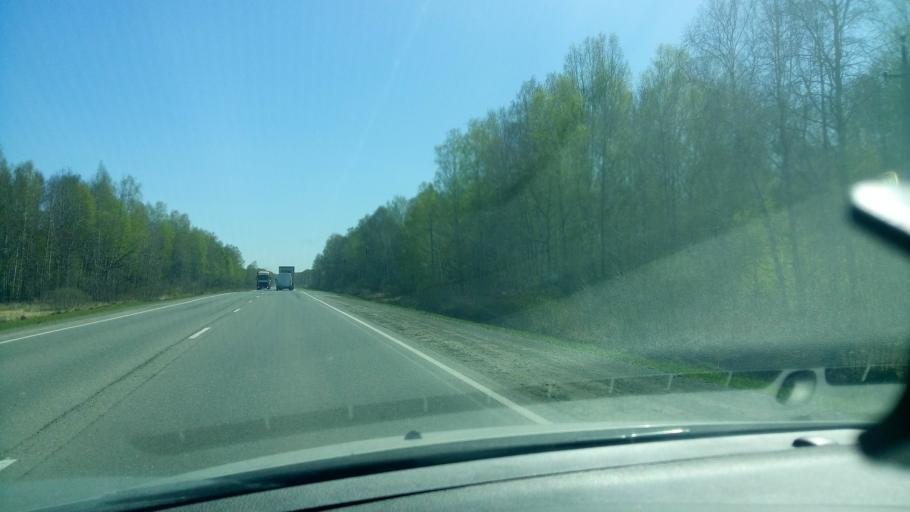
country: RU
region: Sverdlovsk
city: Bogdanovich
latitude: 56.7544
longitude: 62.1802
